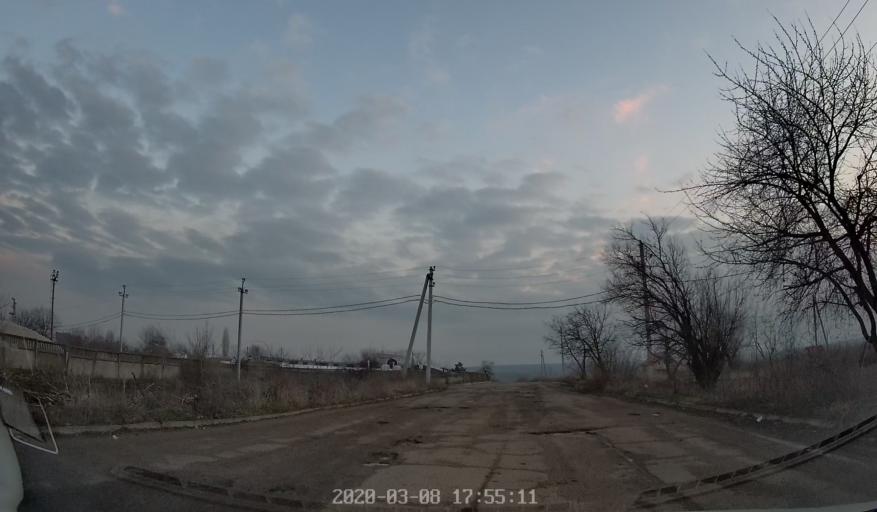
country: MD
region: Rezina
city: Rezina
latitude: 47.7522
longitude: 28.9490
